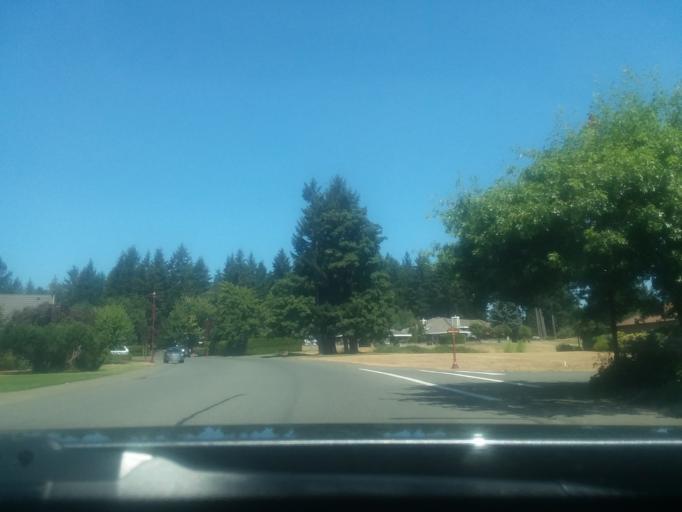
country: CA
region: British Columbia
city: Courtenay
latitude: 49.7103
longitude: -124.9591
